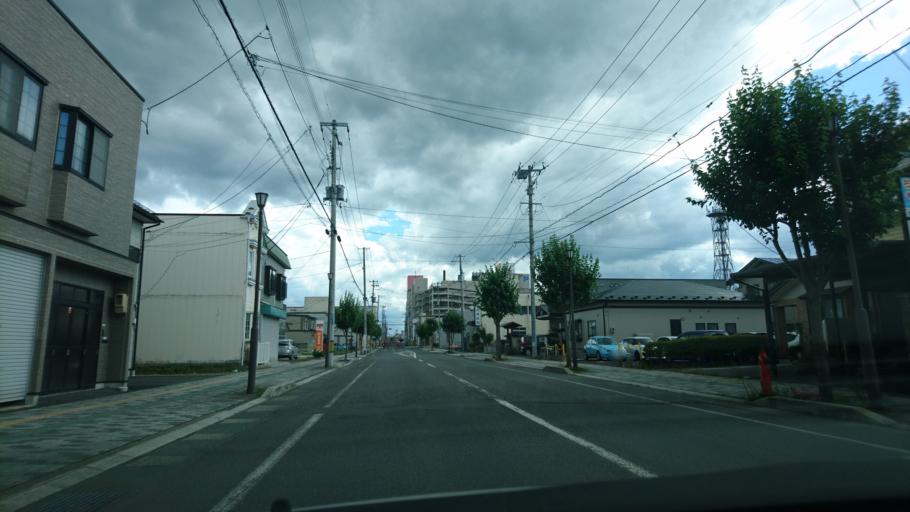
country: JP
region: Iwate
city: Kitakami
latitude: 39.2913
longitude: 141.1186
